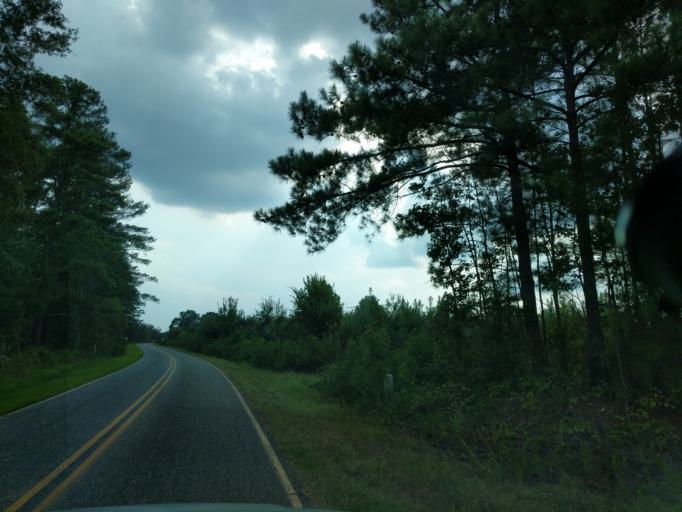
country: US
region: North Carolina
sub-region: Rutherford County
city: Spindale
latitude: 35.2134
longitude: -81.9856
